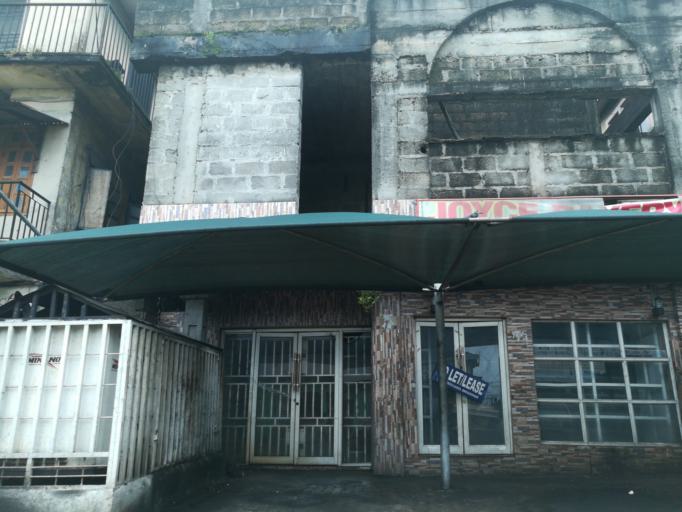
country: NG
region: Rivers
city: Port Harcourt
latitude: 4.7610
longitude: 7.0255
